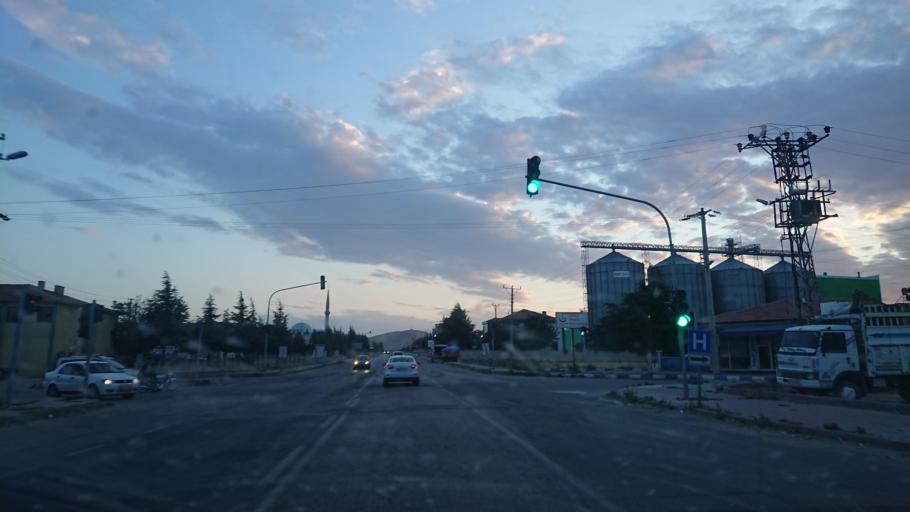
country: TR
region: Aksaray
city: Ortakoy
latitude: 38.7546
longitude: 34.0711
